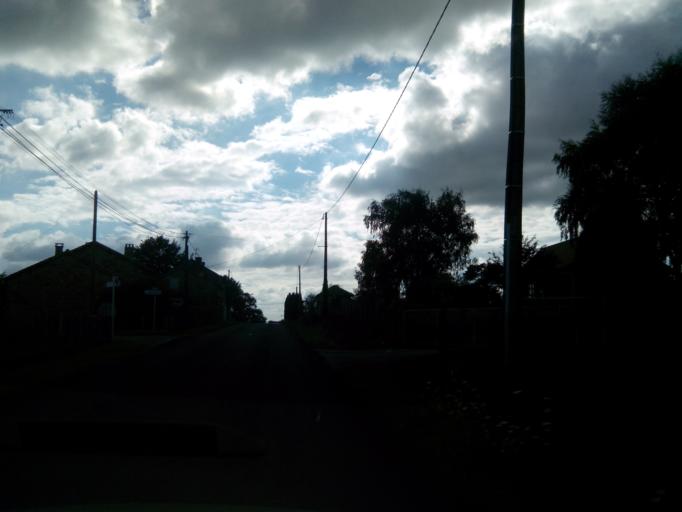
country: FR
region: Limousin
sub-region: Departement de la Haute-Vienne
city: Sauviat-sur-Vige
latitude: 45.8354
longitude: 1.5777
